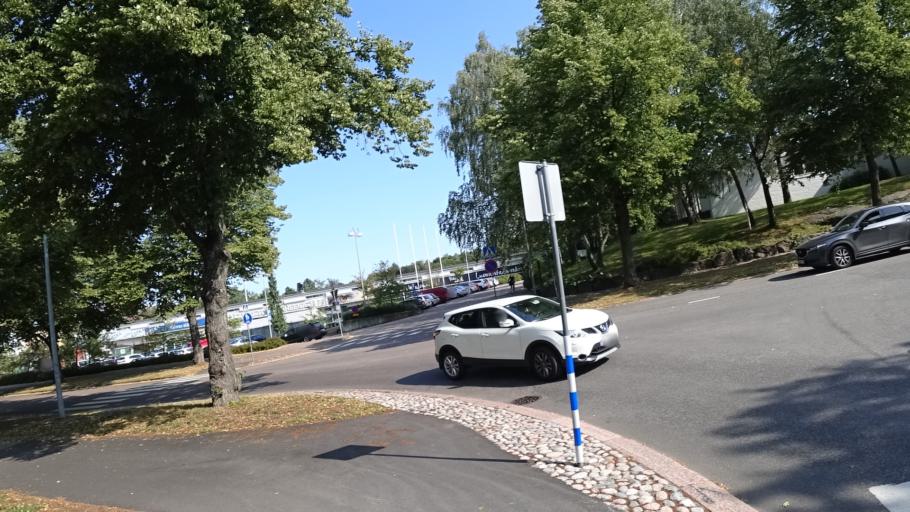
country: FI
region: Kymenlaakso
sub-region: Kotka-Hamina
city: Kotka
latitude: 60.4572
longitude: 26.9369
